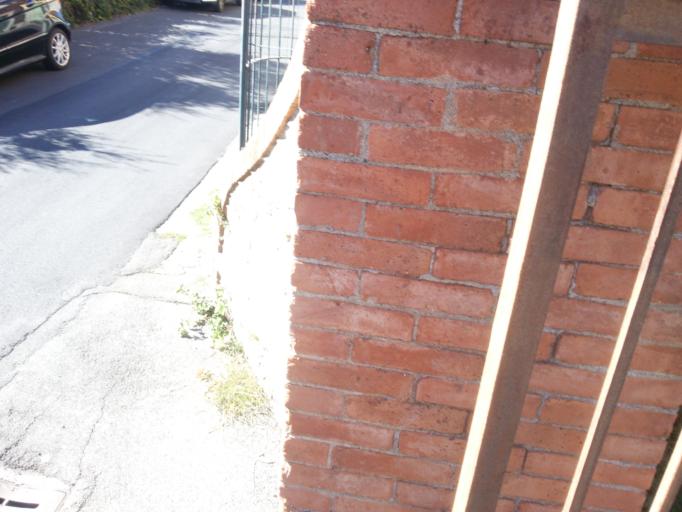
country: IT
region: Liguria
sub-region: Provincia di Genova
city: Chiavari
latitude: 44.3299
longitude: 9.3198
